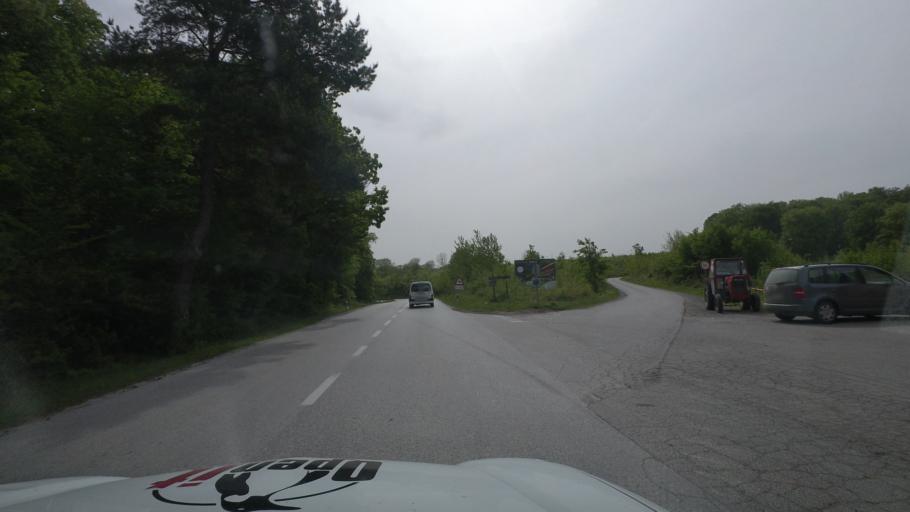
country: HR
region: Karlovacka
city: Vojnic
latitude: 45.3438
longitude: 15.7731
